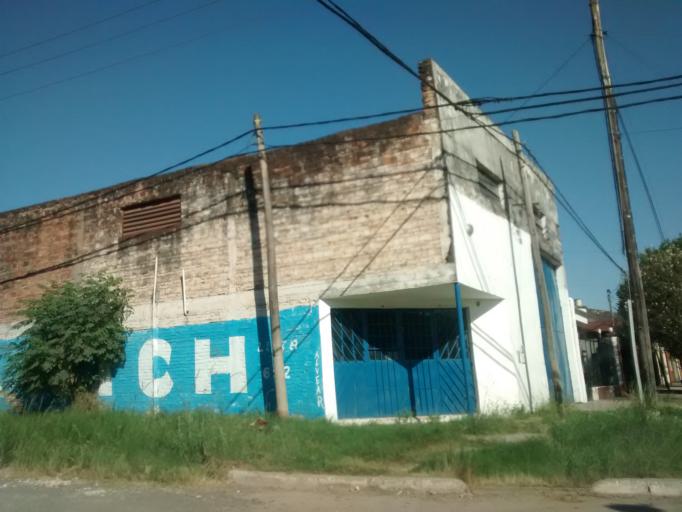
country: AR
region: Chaco
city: Resistencia
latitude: -27.4487
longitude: -59.0014
